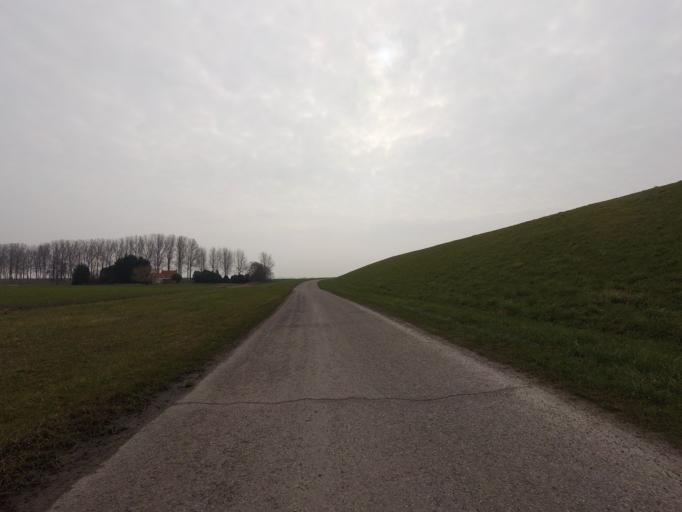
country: BE
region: Flanders
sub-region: Provincie Oost-Vlaanderen
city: Sint-Gillis-Waas
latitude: 51.3368
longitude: 4.1947
